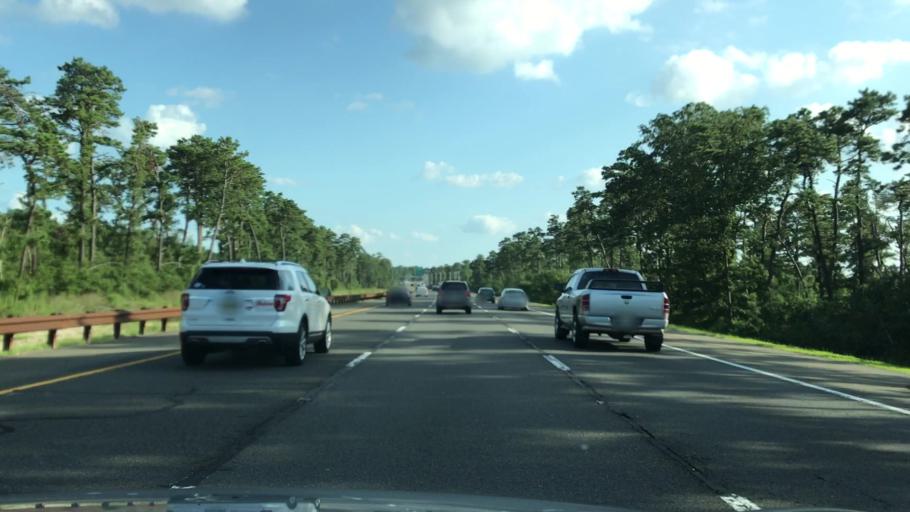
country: US
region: New Jersey
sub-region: Ocean County
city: South Toms River
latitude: 39.9141
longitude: -74.2120
